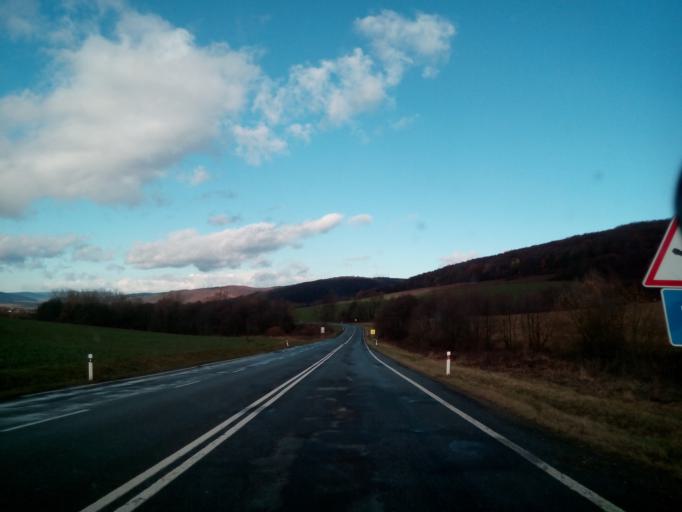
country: SK
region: Presovsky
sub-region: Okres Bardejov
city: Bardejov
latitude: 49.2317
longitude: 21.2847
